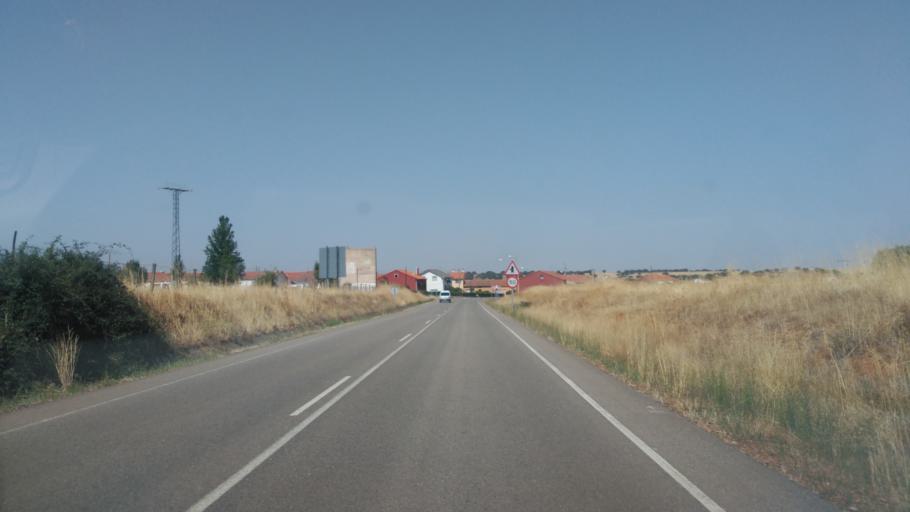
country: ES
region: Castille and Leon
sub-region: Provincia de Salamanca
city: Cabrillas
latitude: 40.7375
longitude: -6.1742
